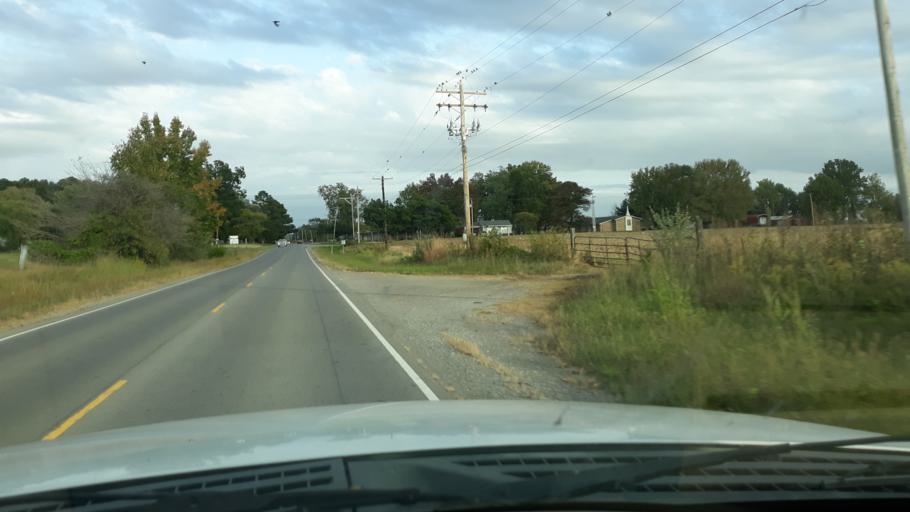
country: US
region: Illinois
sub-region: Saline County
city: Eldorado
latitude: 37.8211
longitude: -88.4870
